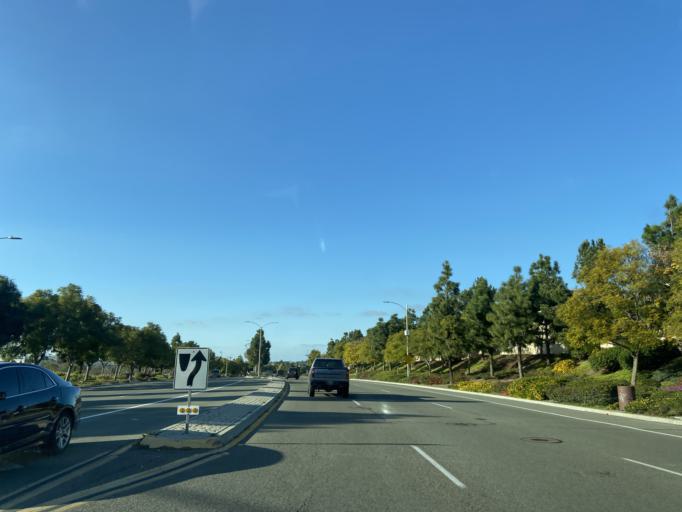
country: US
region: California
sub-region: San Diego County
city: Bonita
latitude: 32.6306
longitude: -116.9652
